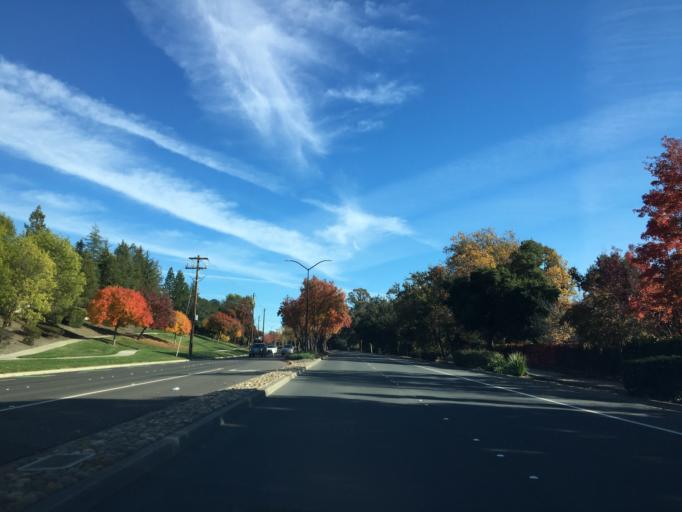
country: US
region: California
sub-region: Contra Costa County
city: Diablo
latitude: 37.8041
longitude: -121.9426
